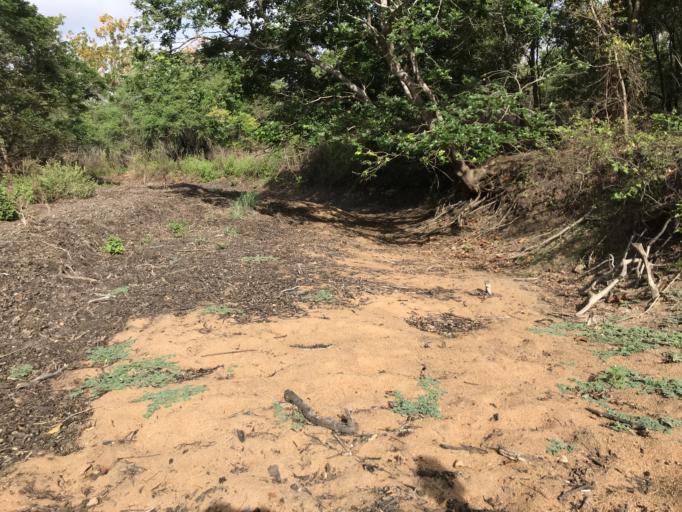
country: LK
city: Padaviya Divisional Secretariat
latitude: 9.0871
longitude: 80.8069
